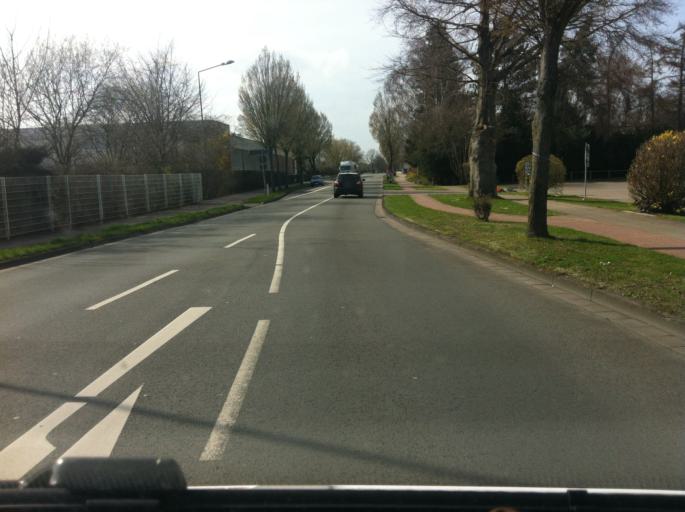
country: DE
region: North Rhine-Westphalia
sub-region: Regierungsbezirk Detmold
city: Minden
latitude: 52.2975
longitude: 8.8802
